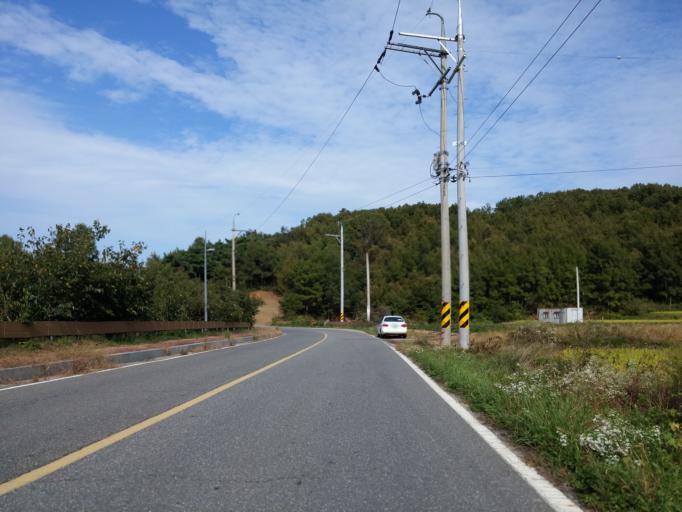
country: KR
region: Chungcheongnam-do
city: Yonmu
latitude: 36.1708
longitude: 127.1622
